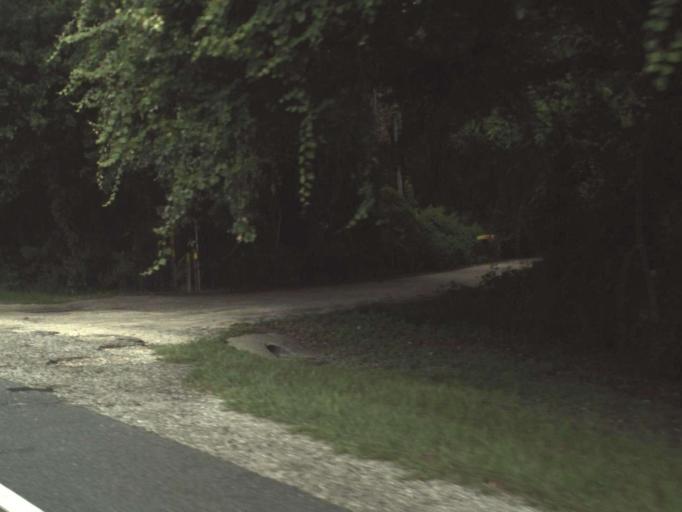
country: US
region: Florida
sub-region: Sumter County
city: Bushnell
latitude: 28.6067
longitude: -82.1401
